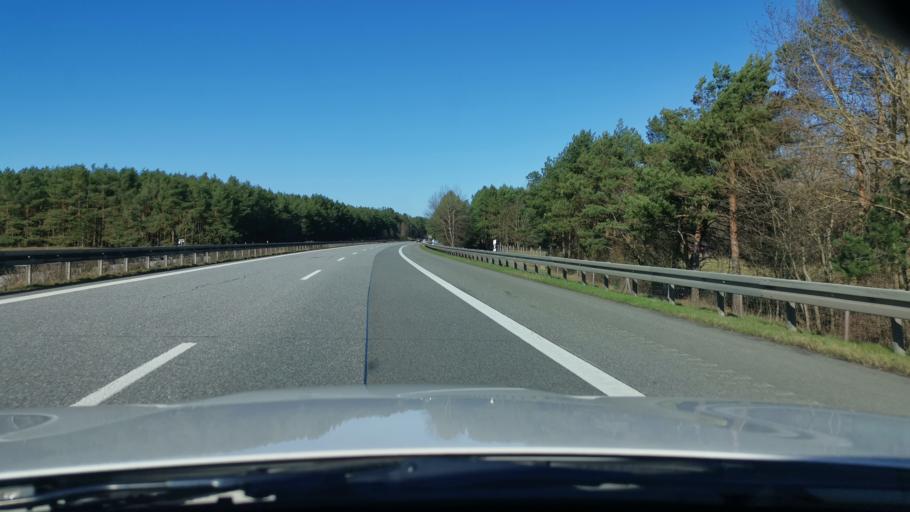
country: DE
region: Mecklenburg-Vorpommern
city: Malchow
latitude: 53.5175
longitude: 12.3572
